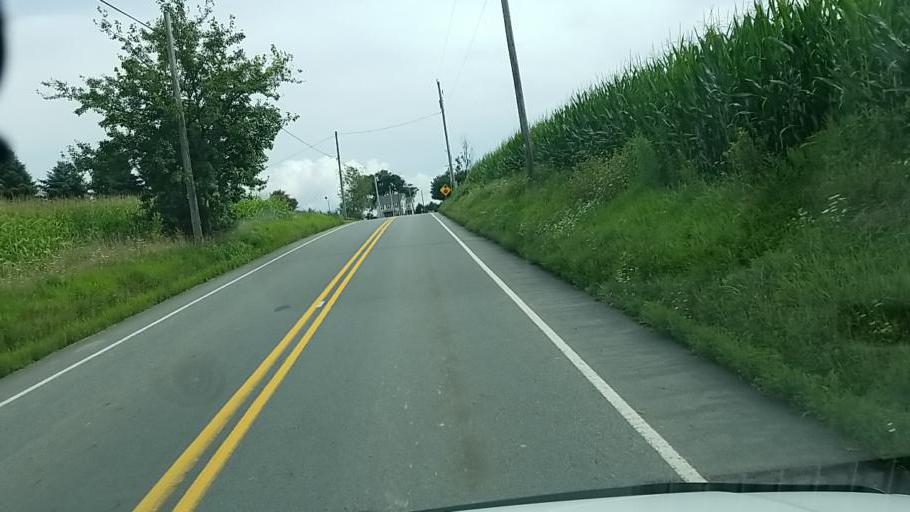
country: US
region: Pennsylvania
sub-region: Dauphin County
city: Elizabethville
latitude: 40.6082
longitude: -76.7791
